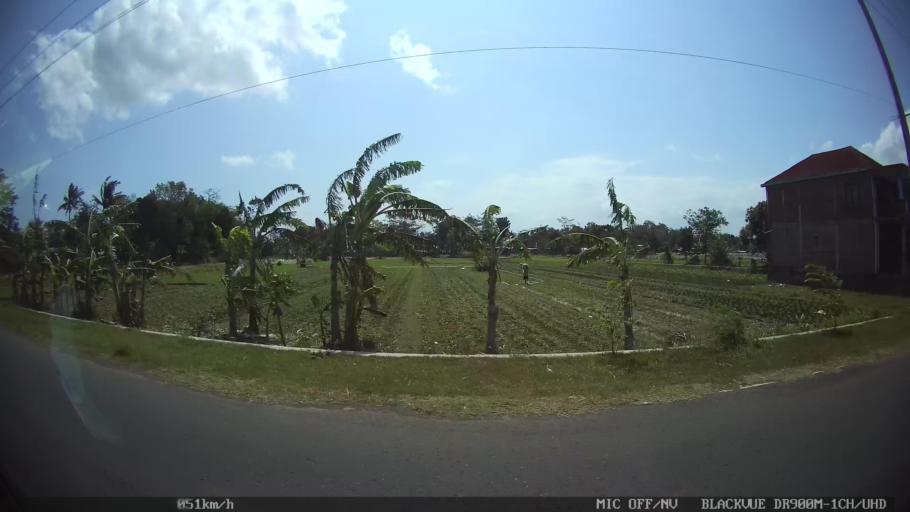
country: ID
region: Daerah Istimewa Yogyakarta
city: Pundong
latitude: -7.9654
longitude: 110.3550
